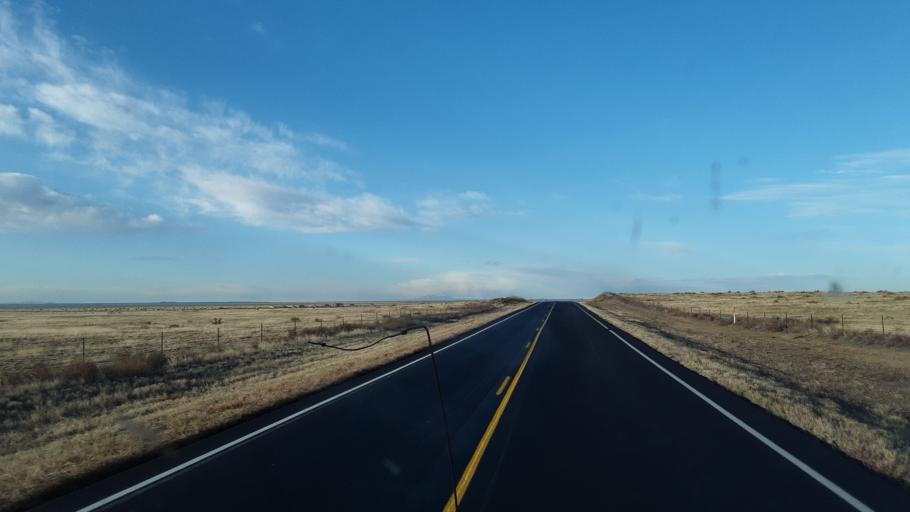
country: US
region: Colorado
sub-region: Otero County
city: Rocky Ford
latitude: 37.9711
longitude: -103.8174
